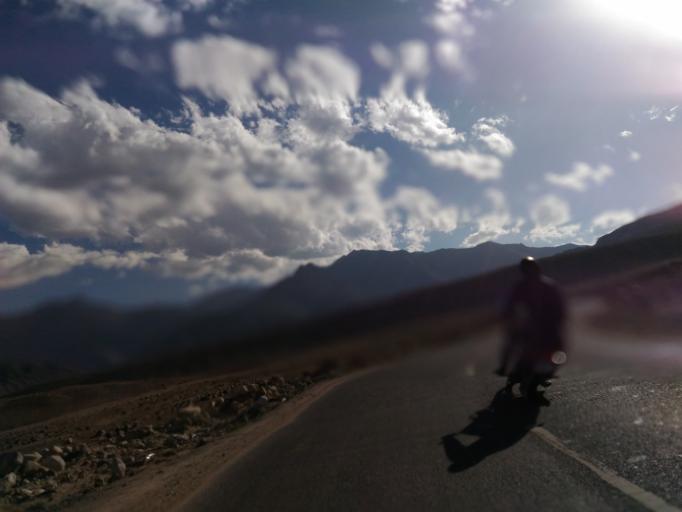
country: IN
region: Kashmir
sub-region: Ladakh
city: Leh
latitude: 34.1596
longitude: 77.4387
